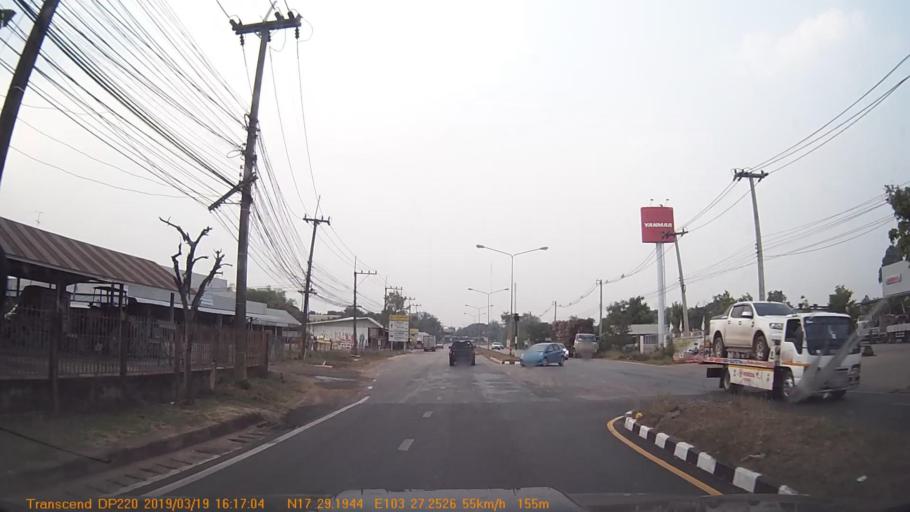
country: TH
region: Sakon Nakhon
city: Sawang Daen Din
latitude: 17.4871
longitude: 103.4540
